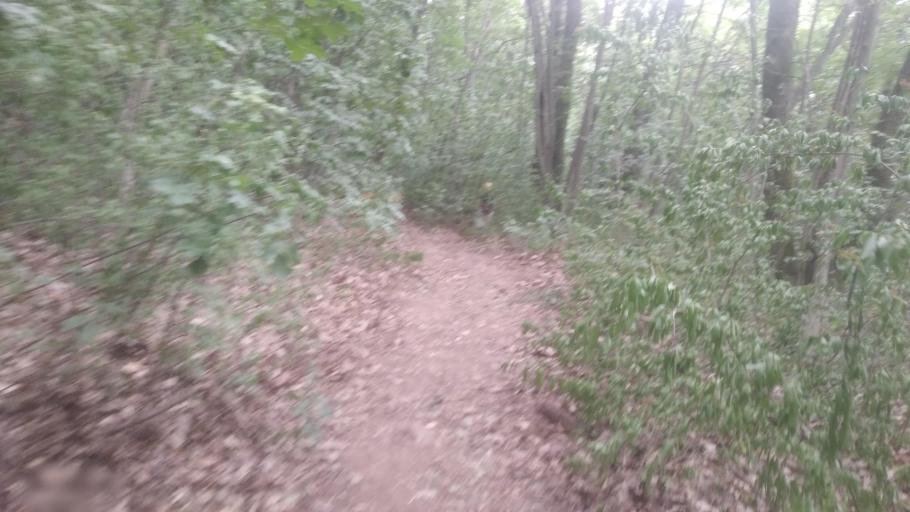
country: HU
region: Veszprem
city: Szentkiralyszabadja
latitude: 47.0078
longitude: 17.9778
